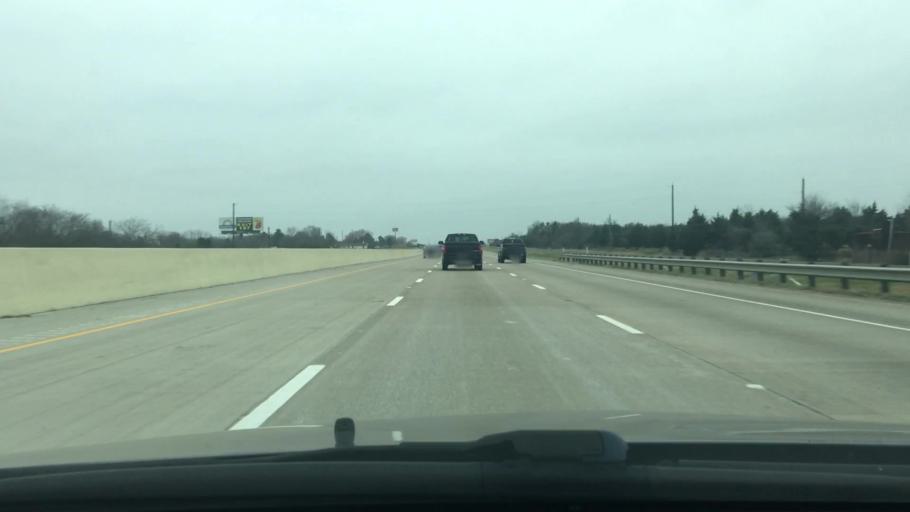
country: US
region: Texas
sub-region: Navarro County
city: Corsicana
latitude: 31.9984
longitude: -96.4299
